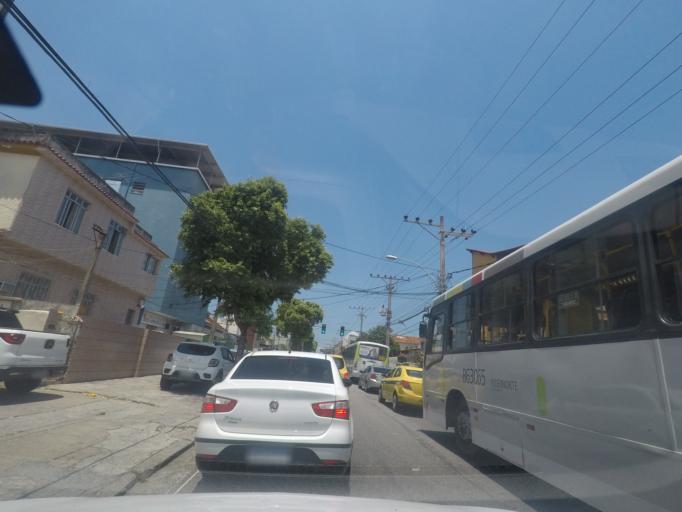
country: BR
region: Rio de Janeiro
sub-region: Duque De Caxias
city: Duque de Caxias
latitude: -22.8401
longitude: -43.3000
